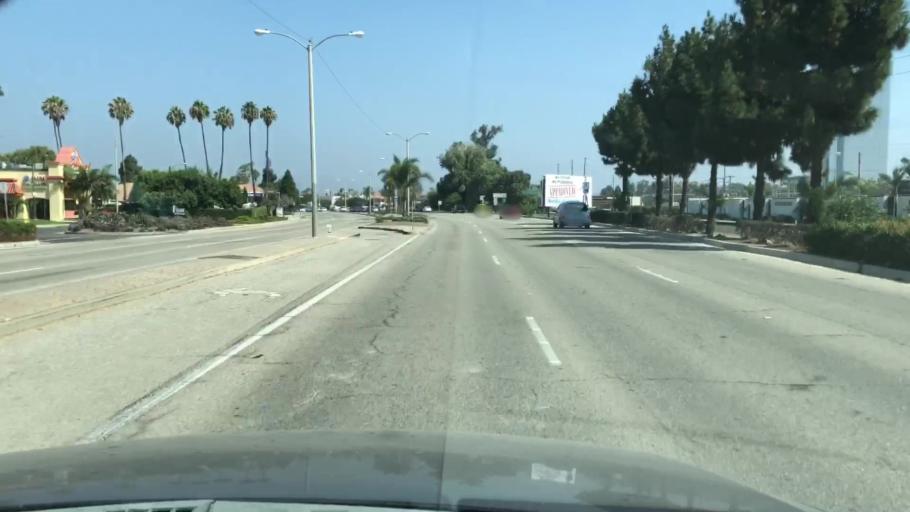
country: US
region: California
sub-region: Ventura County
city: El Rio
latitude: 34.2238
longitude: -119.1770
